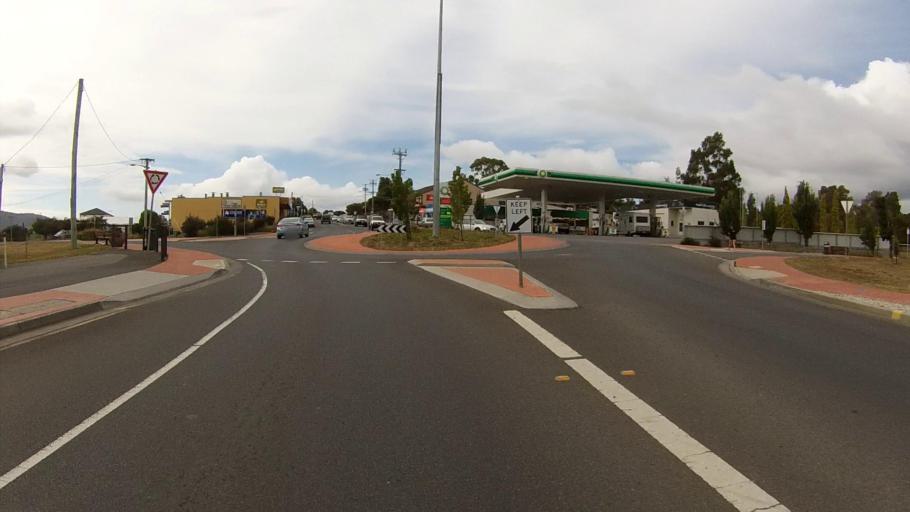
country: AU
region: Tasmania
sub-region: Kingborough
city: Margate
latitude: -43.0260
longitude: 147.2609
